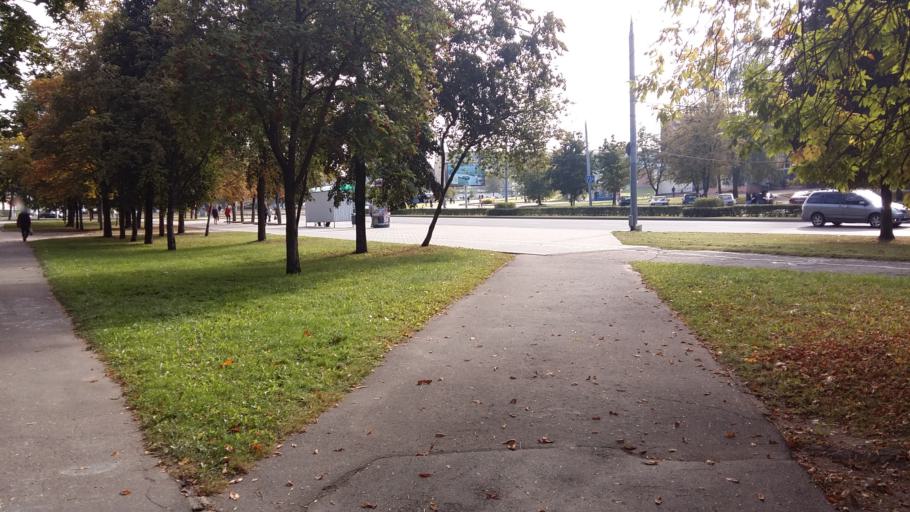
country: BY
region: Grodnenskaya
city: Hrodna
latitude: 53.6995
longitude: 23.8164
